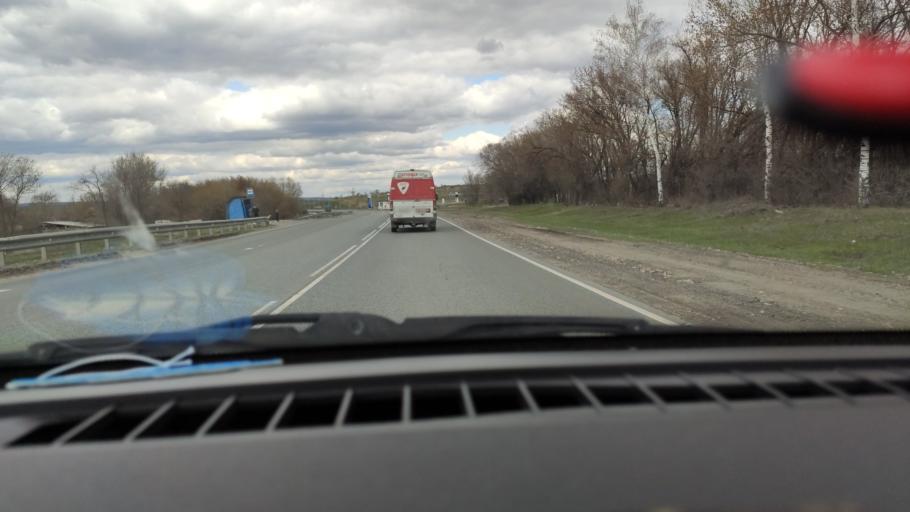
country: RU
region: Saratov
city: Tersa
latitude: 52.0945
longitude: 47.5407
